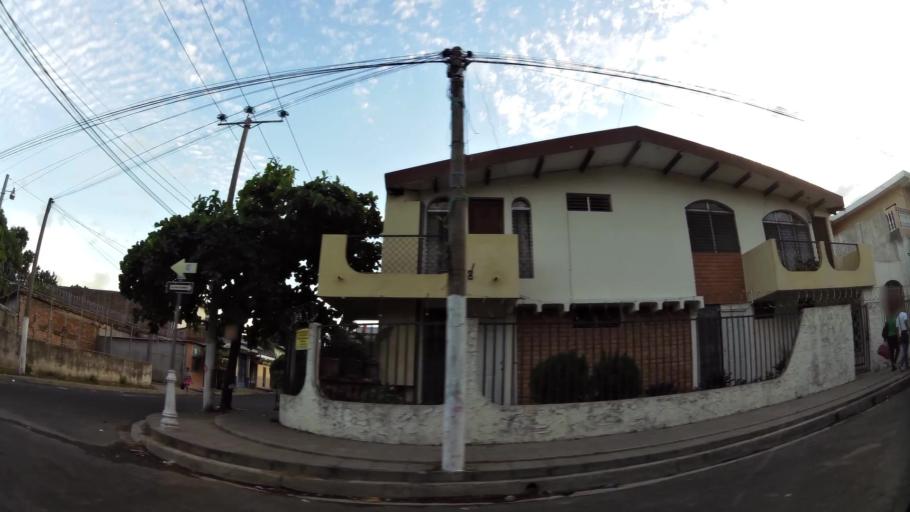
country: SV
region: San Vicente
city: San Vicente
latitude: 13.6463
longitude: -88.7863
